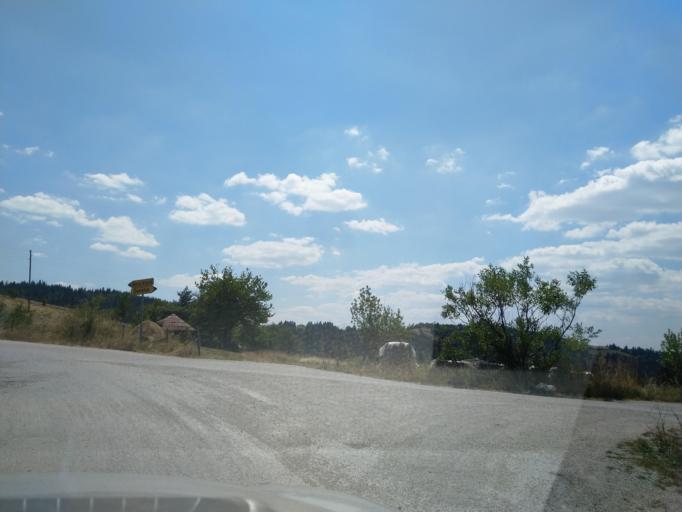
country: RS
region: Central Serbia
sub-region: Zlatiborski Okrug
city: Nova Varos
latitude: 43.4712
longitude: 19.9621
